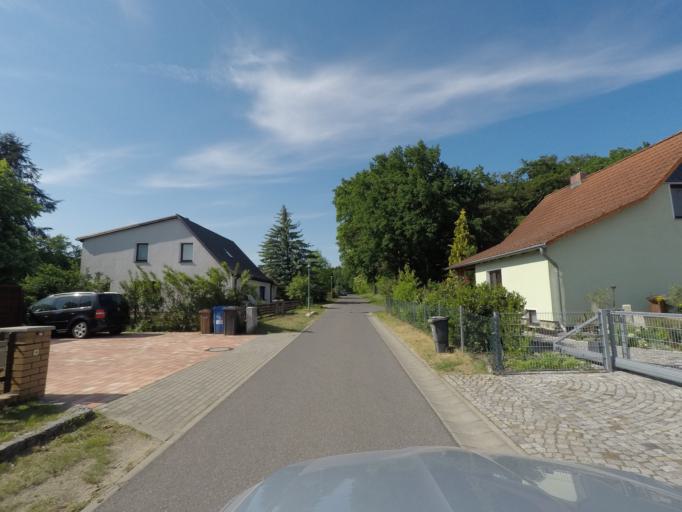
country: DE
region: Brandenburg
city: Melchow
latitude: 52.8629
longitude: 13.7162
